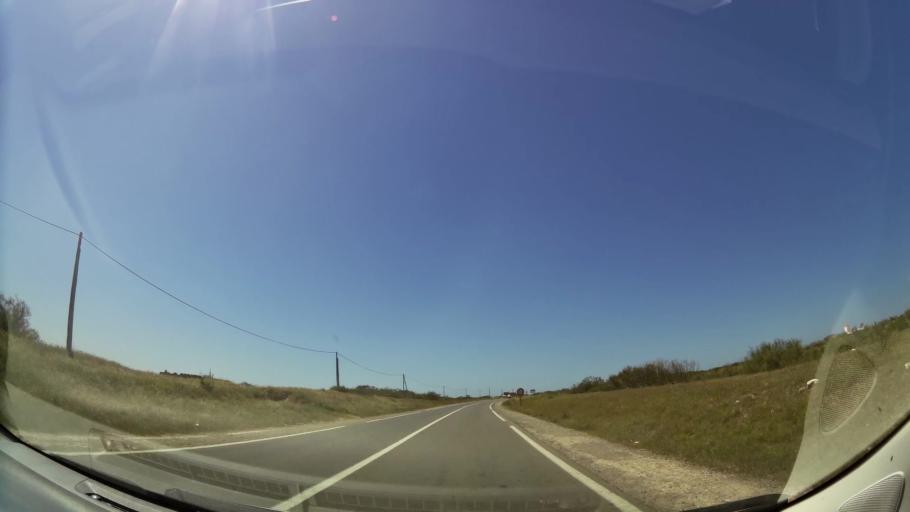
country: MA
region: Oriental
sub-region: Berkane-Taourirt
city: Madagh
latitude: 35.1272
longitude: -2.3926
